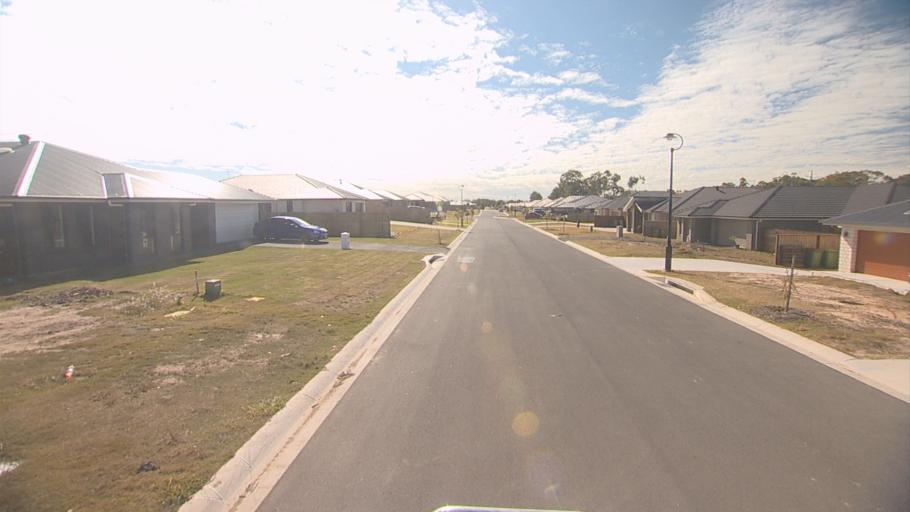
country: AU
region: Queensland
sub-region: Logan
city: Chambers Flat
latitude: -27.7778
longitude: 153.1008
